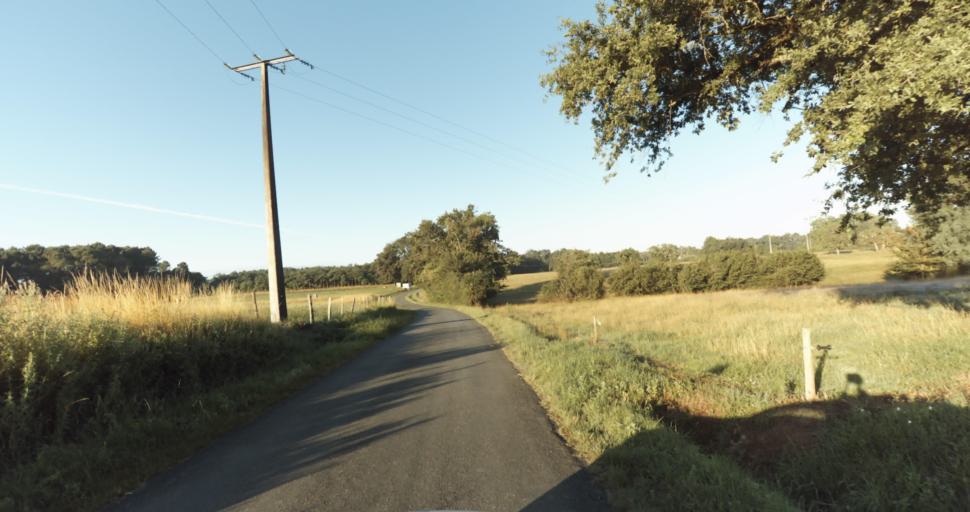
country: FR
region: Aquitaine
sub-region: Departement de la Gironde
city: Bazas
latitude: 44.4211
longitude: -0.2333
